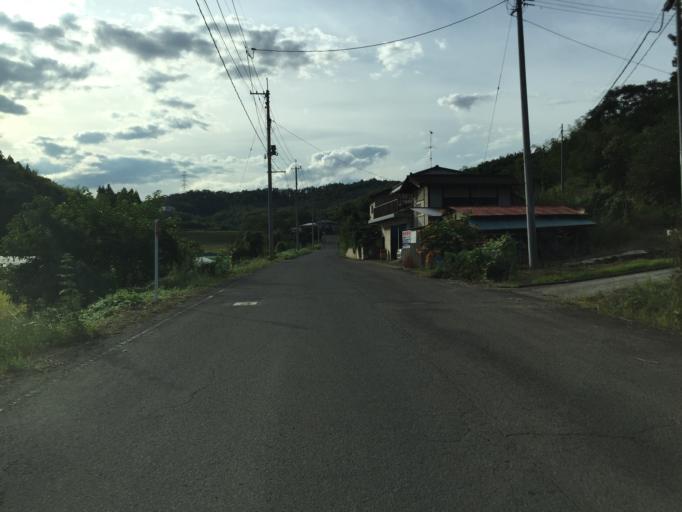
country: JP
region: Fukushima
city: Hobaramachi
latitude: 37.7964
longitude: 140.5327
